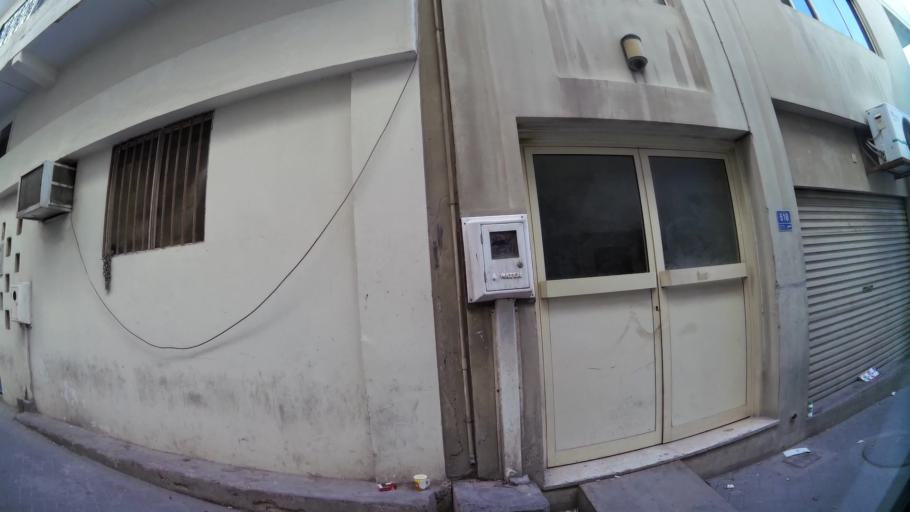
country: BH
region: Manama
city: Manama
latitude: 26.2289
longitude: 50.5750
